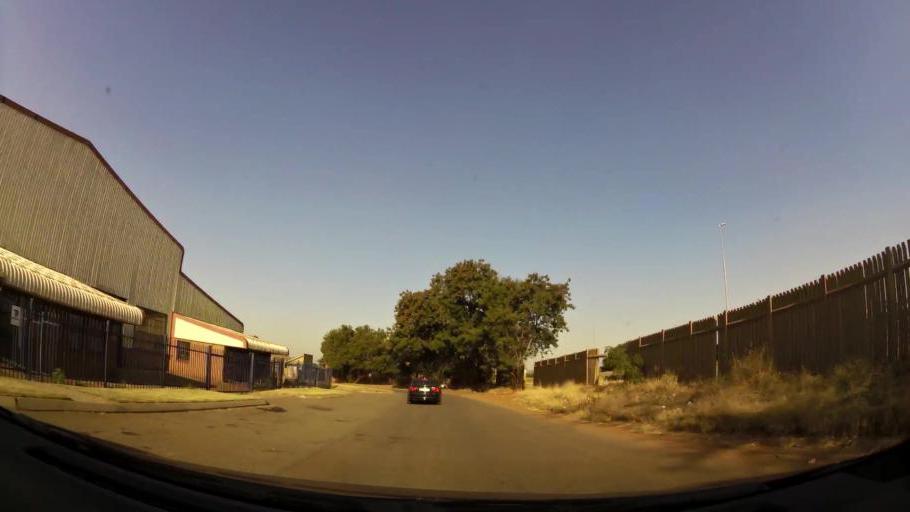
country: ZA
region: North-West
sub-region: Bojanala Platinum District Municipality
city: Rustenburg
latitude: -25.6507
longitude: 27.2165
